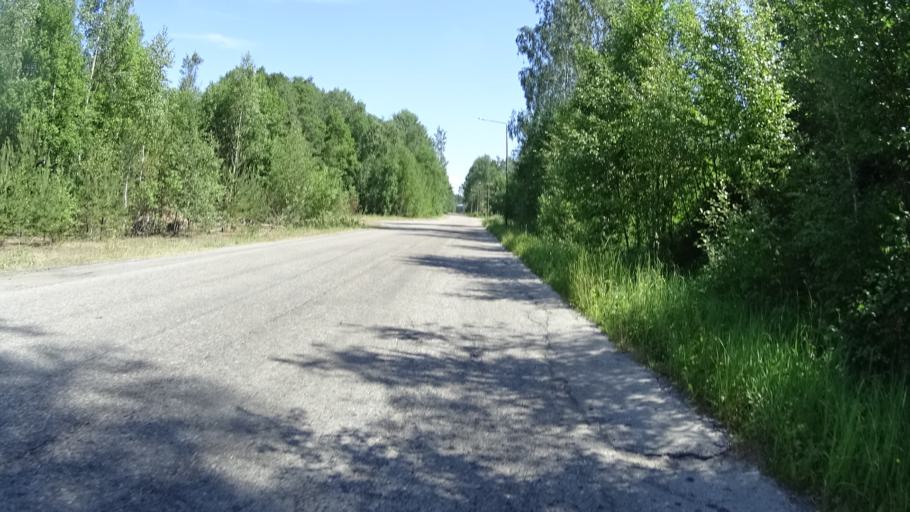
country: FI
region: Uusimaa
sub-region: Raaseporin
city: Pohja
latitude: 60.0935
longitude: 23.5758
